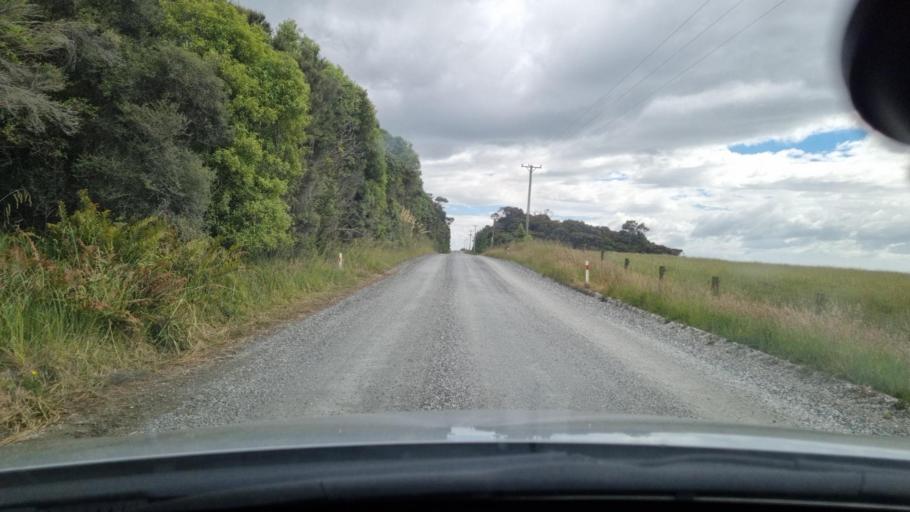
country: NZ
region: Southland
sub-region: Invercargill City
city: Bluff
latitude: -46.5297
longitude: 168.2686
